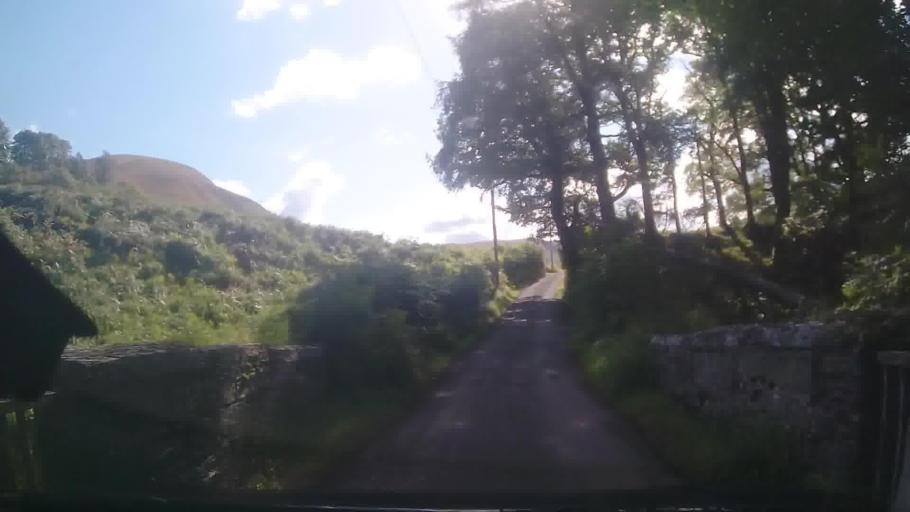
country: GB
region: Wales
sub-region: Gwynedd
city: Bala
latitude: 52.7734
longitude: -3.6233
